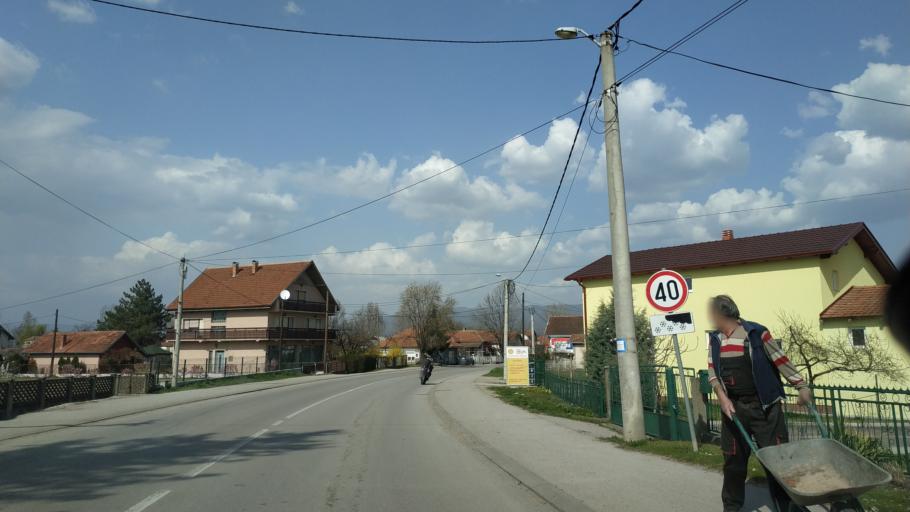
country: RS
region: Central Serbia
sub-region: Nisavski Okrug
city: Aleksinac
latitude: 43.5131
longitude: 21.6974
